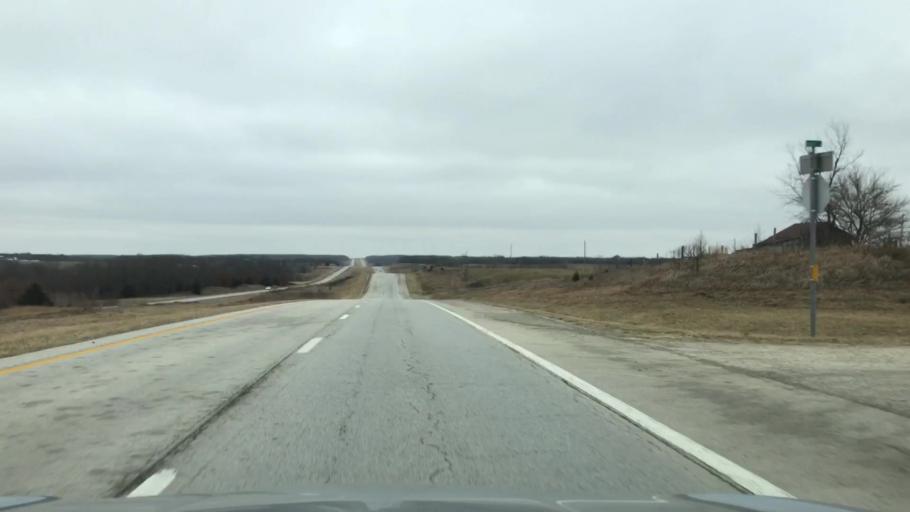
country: US
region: Missouri
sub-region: Linn County
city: Marceline
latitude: 39.7592
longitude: -92.8846
